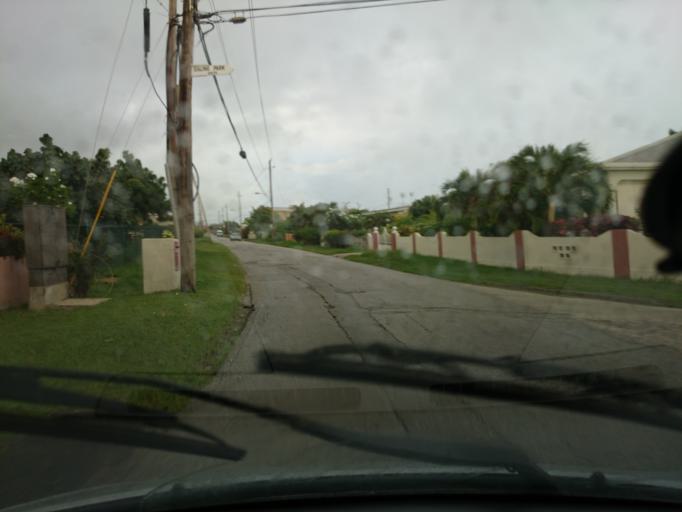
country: BB
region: Christ Church
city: Oistins
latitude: 13.0581
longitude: -59.5138
